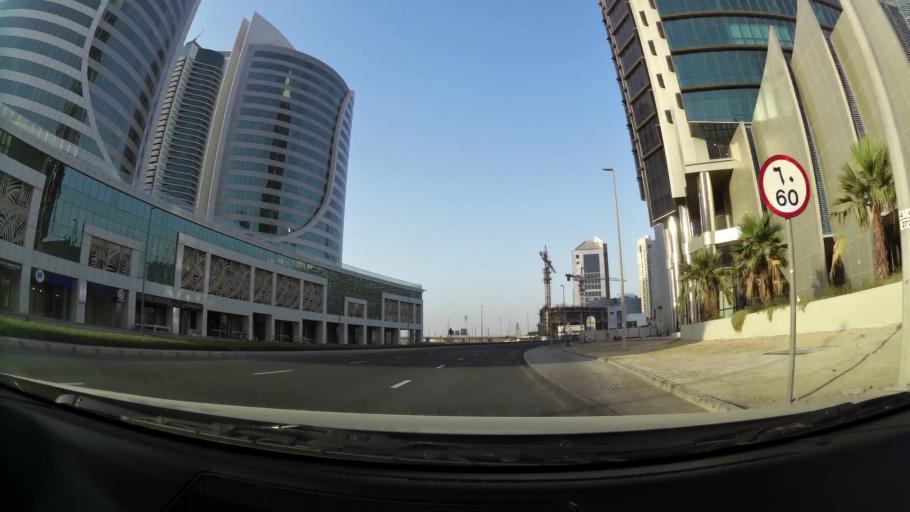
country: AE
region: Dubai
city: Dubai
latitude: 25.1912
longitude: 55.2849
